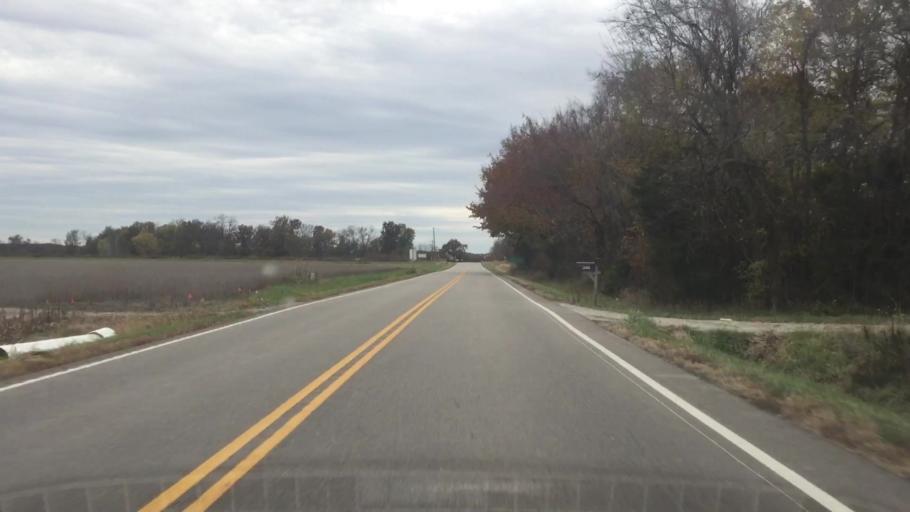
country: US
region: Missouri
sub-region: Callaway County
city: Holts Summit
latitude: 38.6061
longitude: -91.9894
